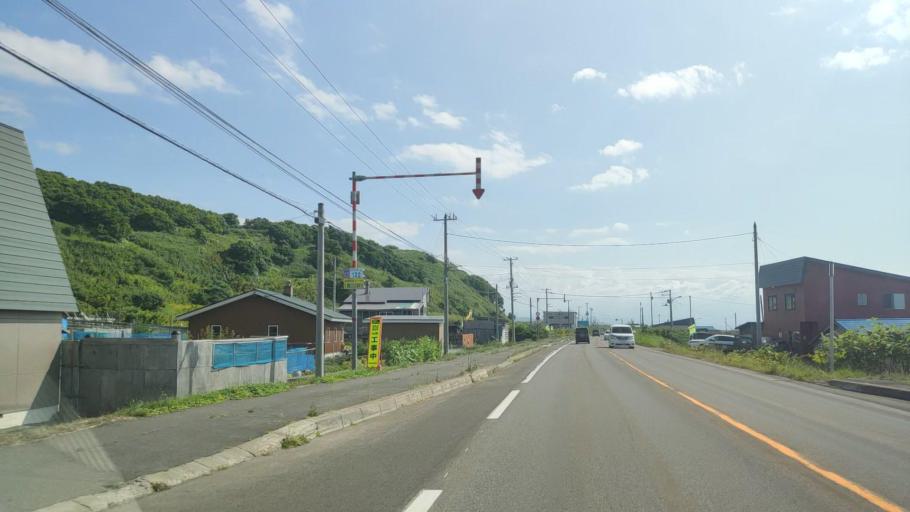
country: JP
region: Hokkaido
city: Rumoi
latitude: 43.9832
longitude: 141.6479
